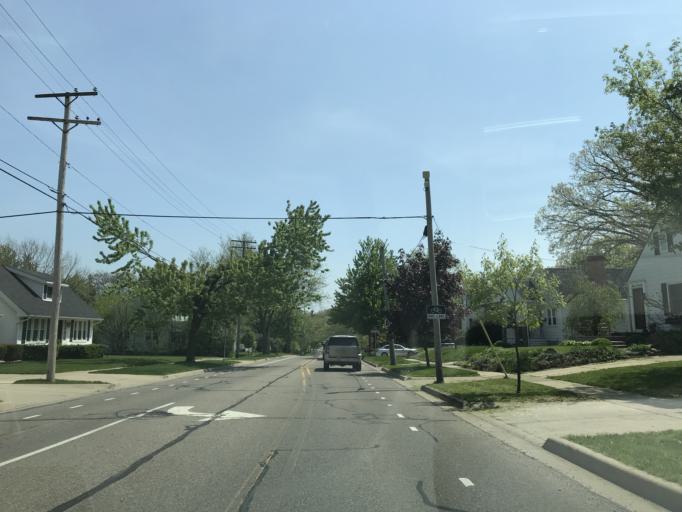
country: US
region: Michigan
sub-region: Washtenaw County
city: Ann Arbor
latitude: 42.2681
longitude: -83.7583
